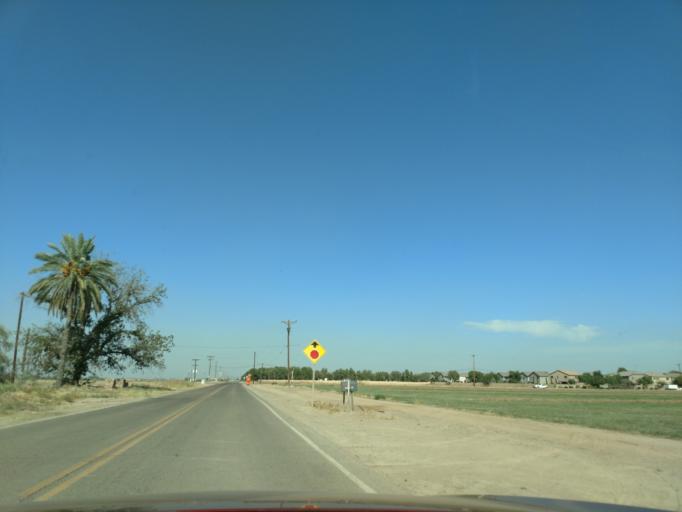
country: US
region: Arizona
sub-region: Maricopa County
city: Laveen
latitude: 33.3612
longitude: -112.1863
